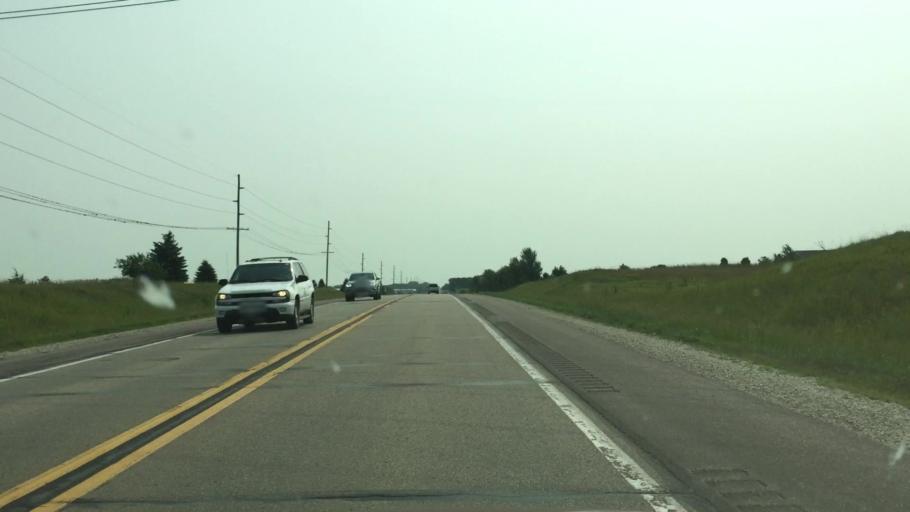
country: US
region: Iowa
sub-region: Dickinson County
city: Milford
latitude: 43.3424
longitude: -95.1721
